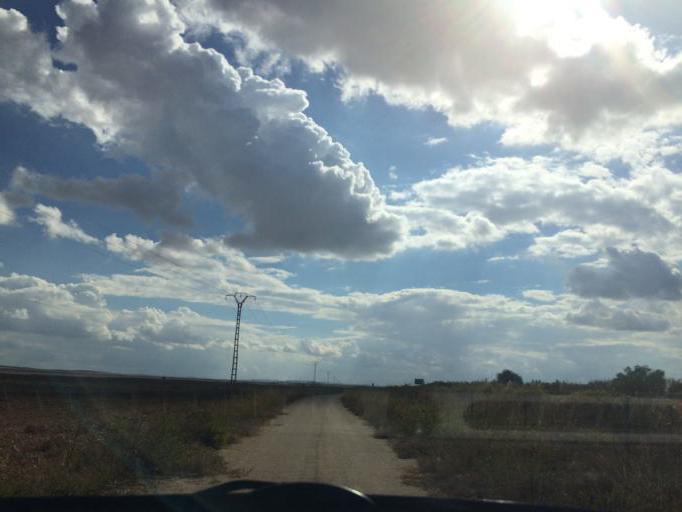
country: ES
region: Castille-La Mancha
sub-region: Provincia de Albacete
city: Albacete
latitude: 38.9564
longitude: -1.8217
